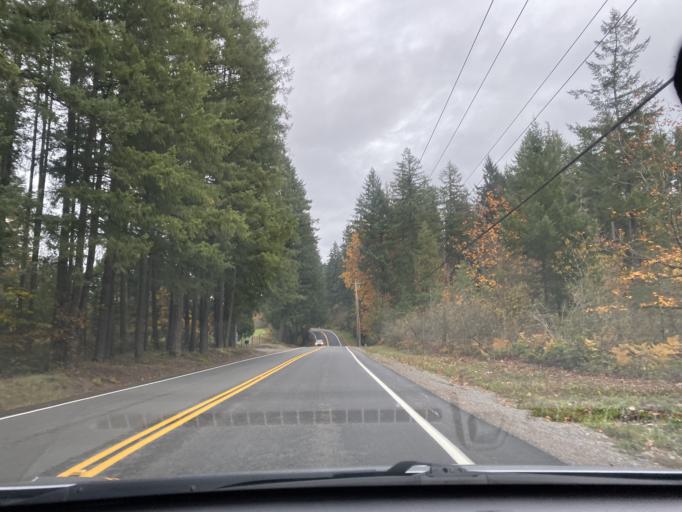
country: US
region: Washington
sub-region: King County
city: Lake Morton-Berrydale
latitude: 47.3000
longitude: -122.0982
